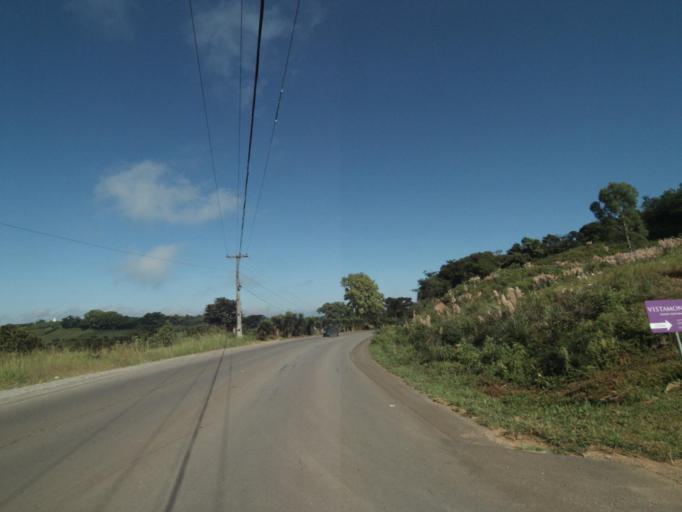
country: BR
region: Rio Grande do Sul
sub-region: Bento Goncalves
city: Bento Goncalves
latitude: -29.1153
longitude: -51.5790
